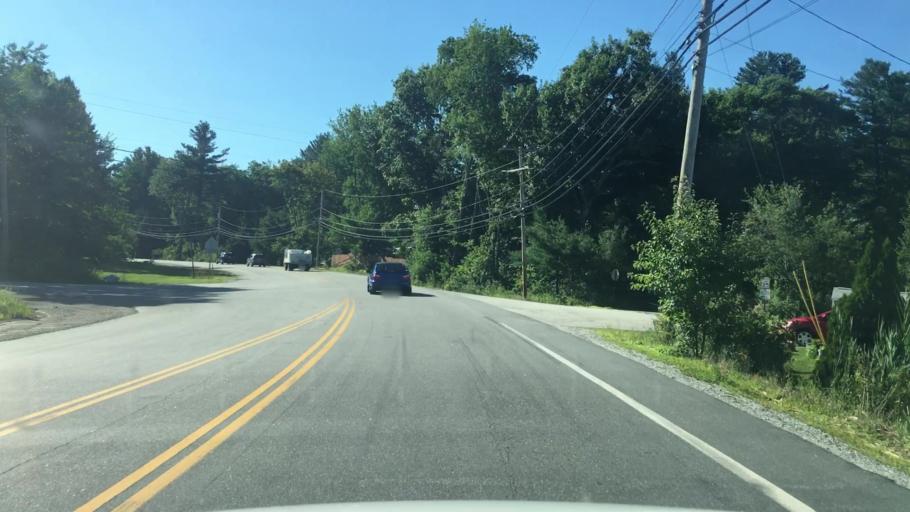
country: US
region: New Hampshire
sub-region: Rockingham County
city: Exeter
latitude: 43.0132
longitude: -71.0077
